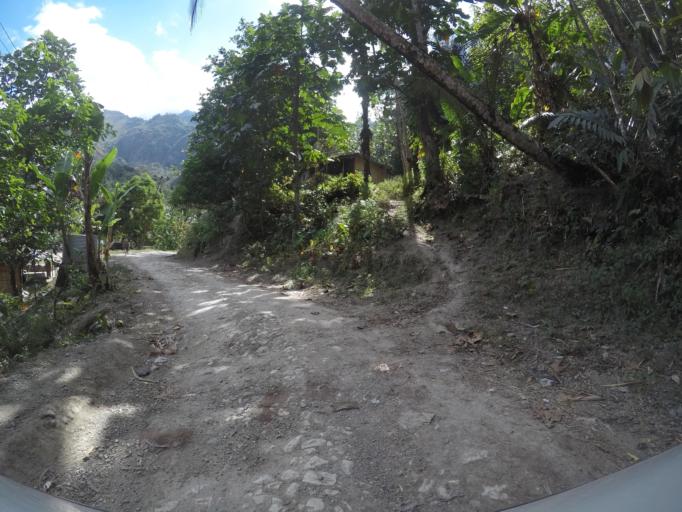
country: TL
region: Baucau
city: Baucau
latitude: -8.6199
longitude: 126.6589
